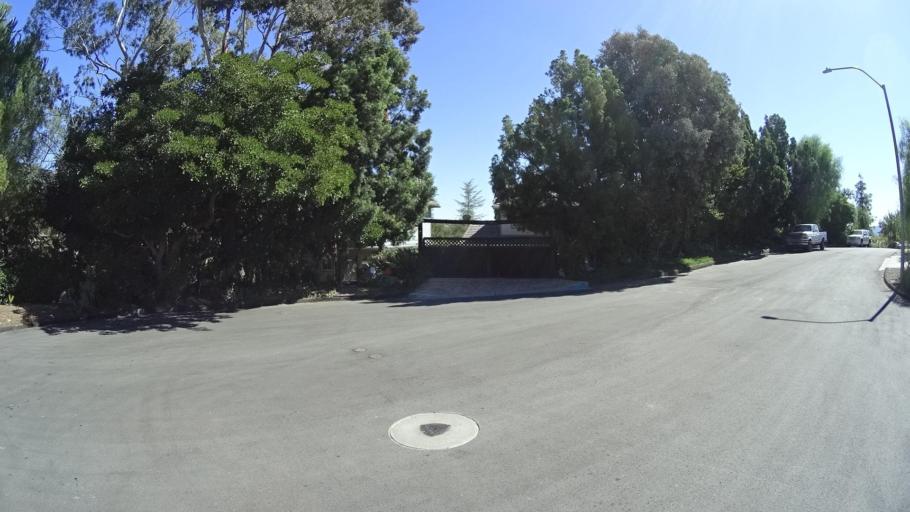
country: US
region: California
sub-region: San Diego County
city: Alpine
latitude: 32.8420
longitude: -116.7637
